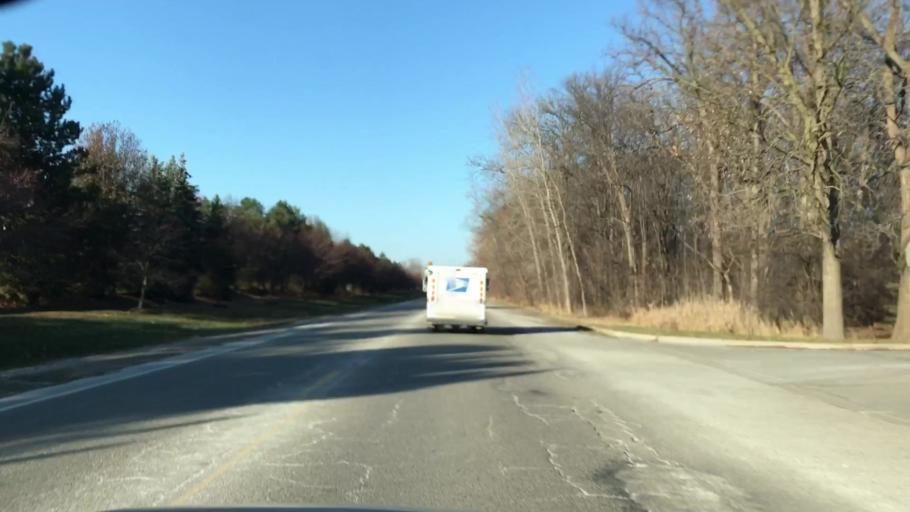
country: US
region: Michigan
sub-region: Oakland County
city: Novi
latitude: 42.4682
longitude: -83.5143
